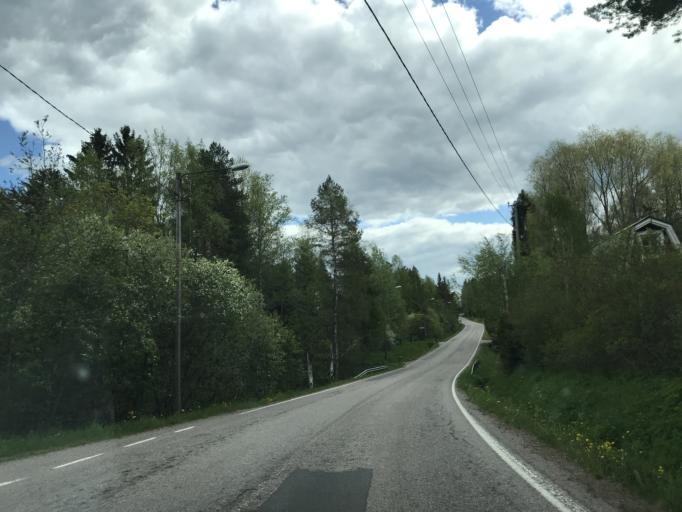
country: FI
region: Uusimaa
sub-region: Helsinki
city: Nurmijaervi
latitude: 60.4302
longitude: 24.7113
